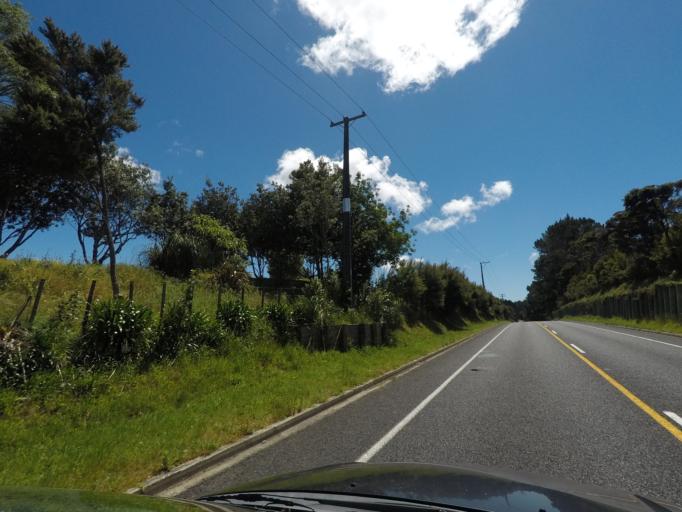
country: NZ
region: Auckland
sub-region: Auckland
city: Rothesay Bay
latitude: -36.7475
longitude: 174.6713
